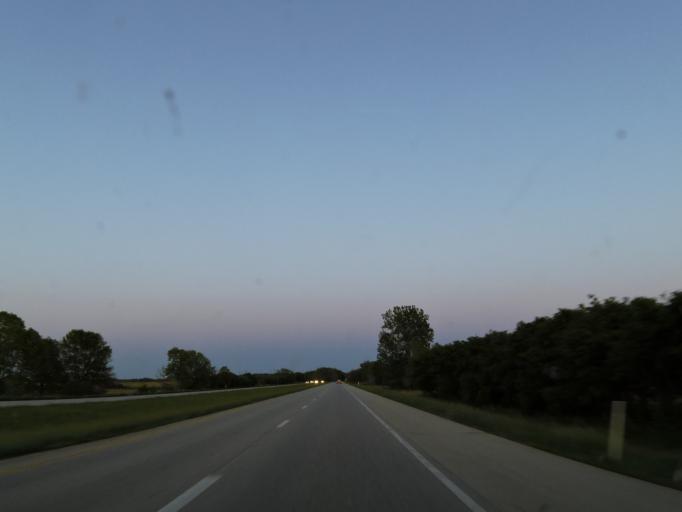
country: US
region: Indiana
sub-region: Boone County
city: Thorntown
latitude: 39.9769
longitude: -86.6707
